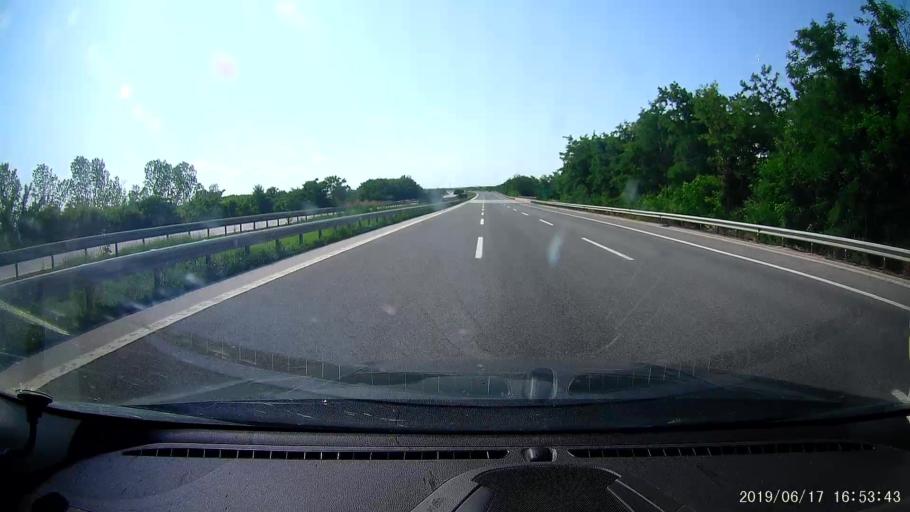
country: TR
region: Kirklareli
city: Inece
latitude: 41.5670
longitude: 27.0161
